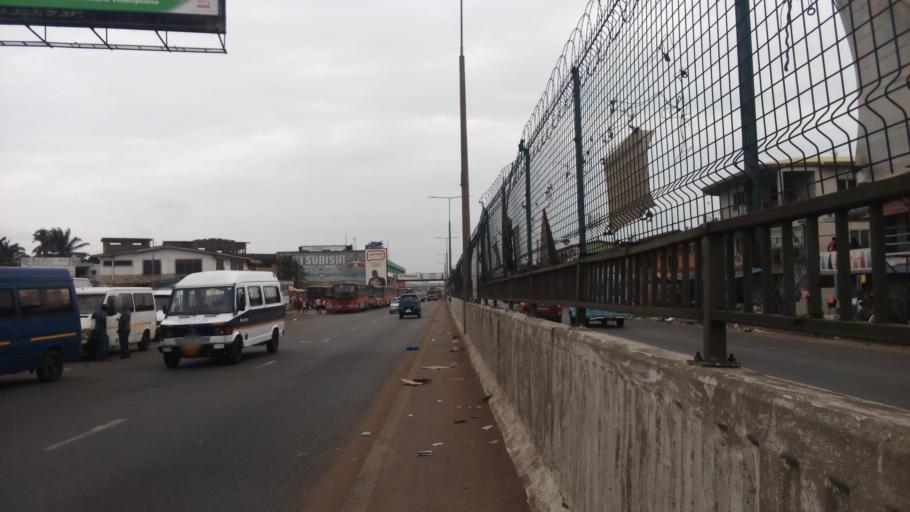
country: GH
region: Greater Accra
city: Accra
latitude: 5.5672
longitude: -0.2391
